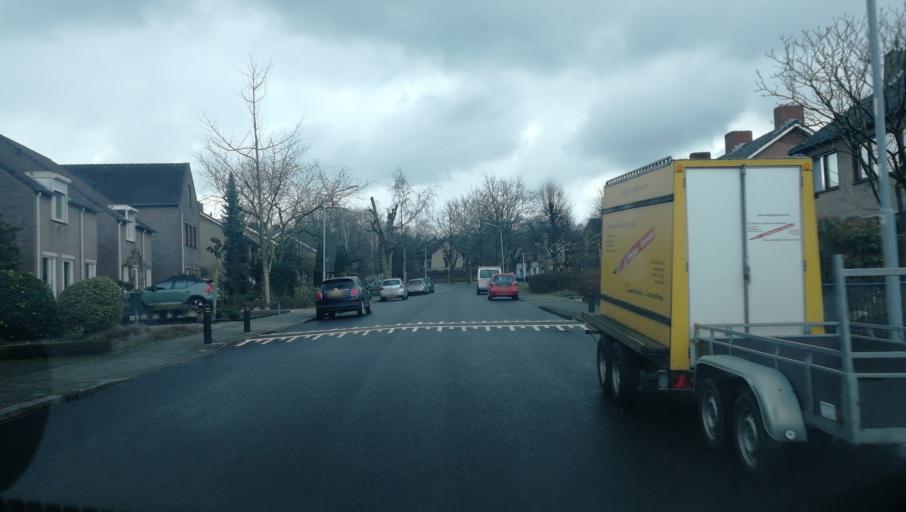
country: NL
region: Limburg
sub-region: Gemeente Venlo
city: Venlo
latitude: 51.3654
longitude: 6.1877
